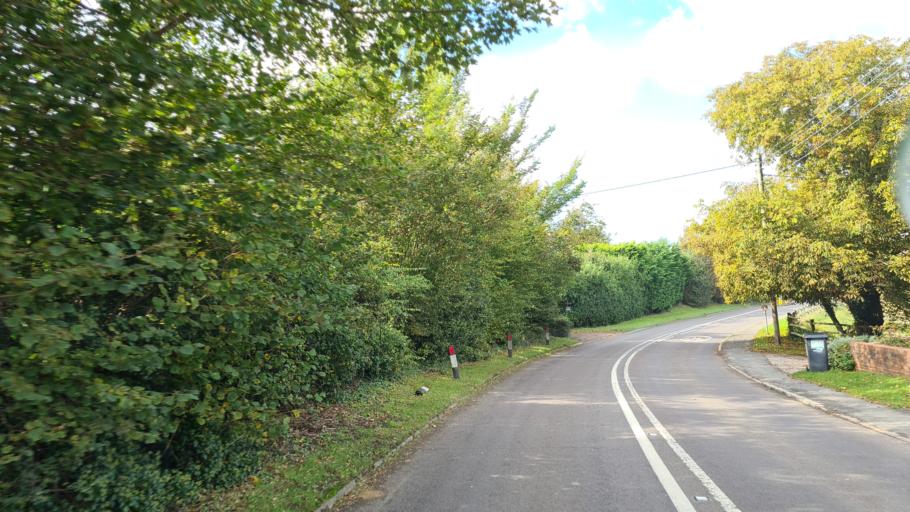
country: GB
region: England
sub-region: East Sussex
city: Bodle Street
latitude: 50.8773
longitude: 0.3656
